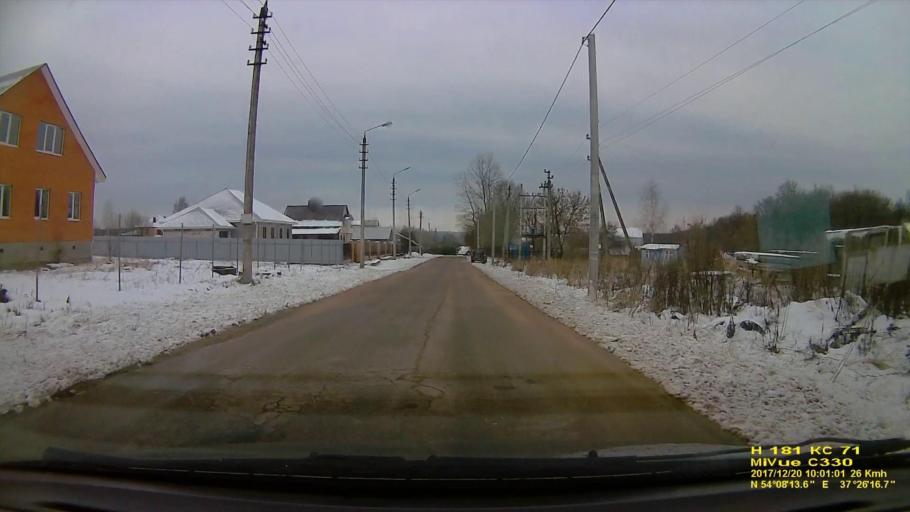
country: RU
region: Tula
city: Kosaya Gora
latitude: 54.1370
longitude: 37.4380
